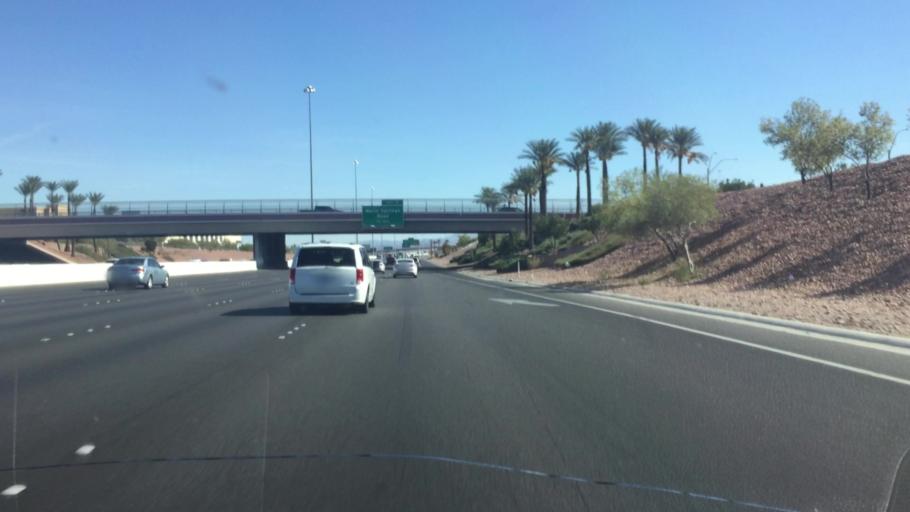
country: US
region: Nevada
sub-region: Clark County
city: Paradise
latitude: 36.0635
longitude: -115.1649
